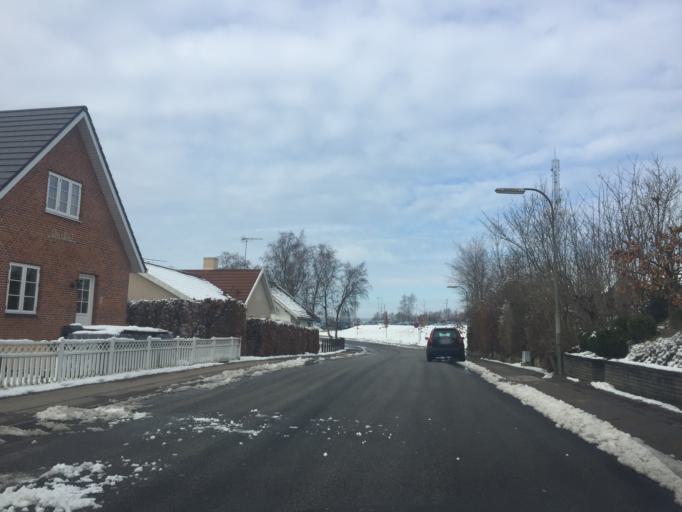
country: DK
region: Capital Region
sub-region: Gribskov Kommune
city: Helsinge
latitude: 56.0229
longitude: 12.1885
